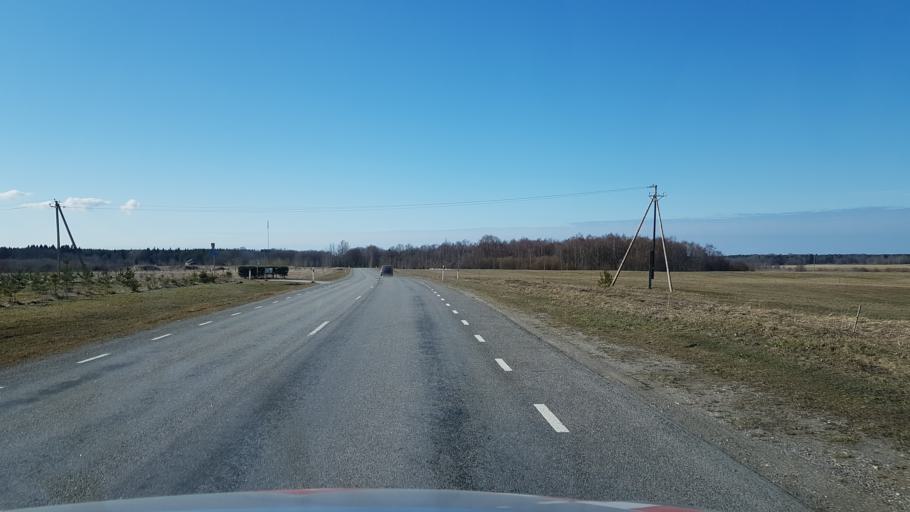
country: EE
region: Laeaene-Virumaa
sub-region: Haljala vald
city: Haljala
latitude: 59.4477
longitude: 26.2487
